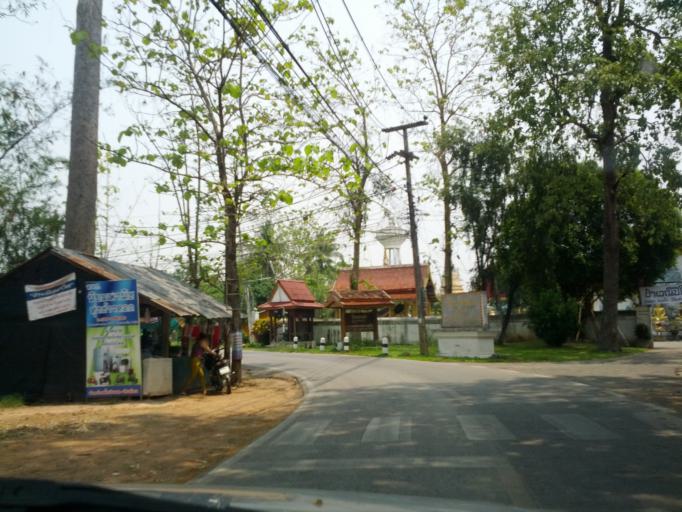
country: TH
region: Chiang Mai
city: San Sai
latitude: 18.8763
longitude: 99.0975
